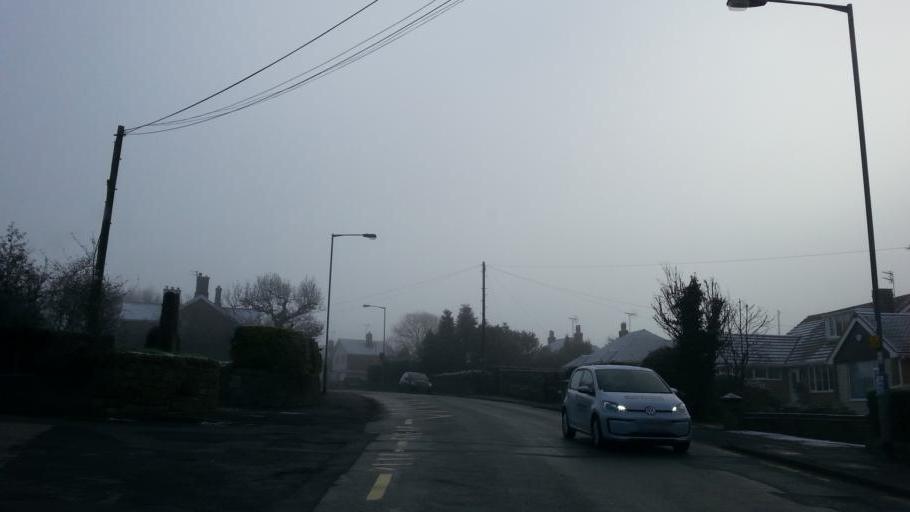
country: GB
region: England
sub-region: Staffordshire
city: Biddulph
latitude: 53.1249
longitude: -2.1632
